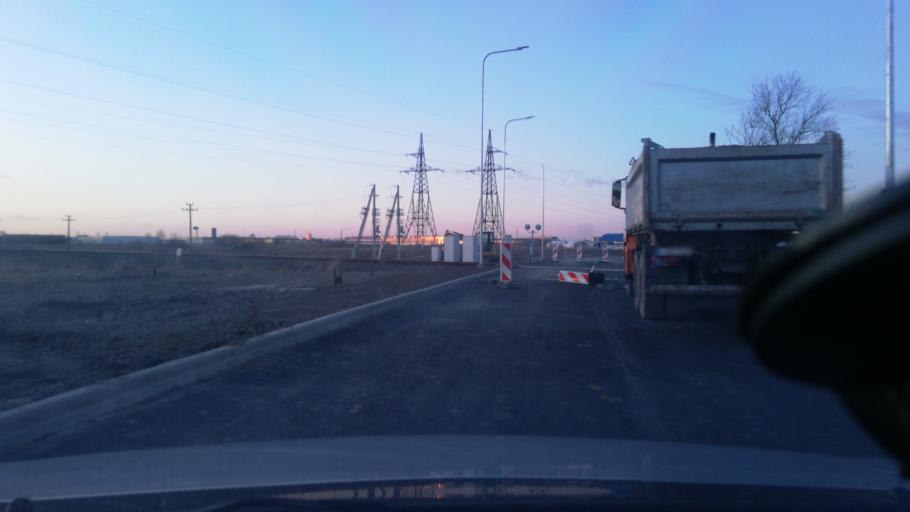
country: LT
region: Klaipedos apskritis
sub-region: Klaipeda
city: Klaipeda
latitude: 55.6831
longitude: 21.1971
